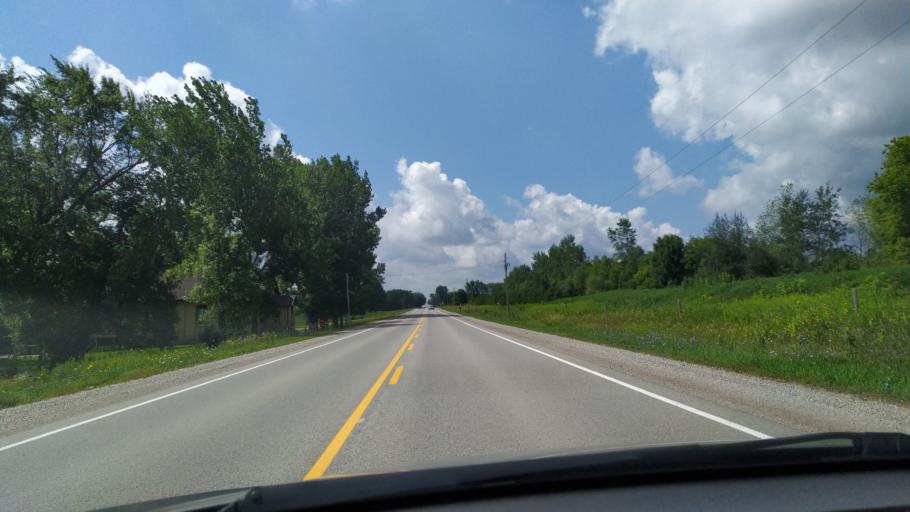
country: CA
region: Ontario
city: South Huron
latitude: 43.3331
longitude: -81.3061
